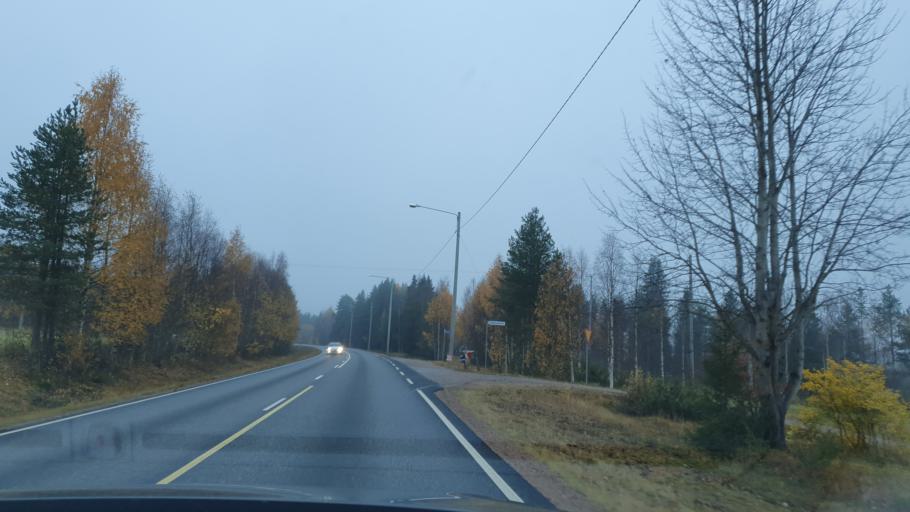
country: FI
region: Lapland
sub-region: Tunturi-Lappi
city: Kittilae
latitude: 67.0321
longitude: 25.1076
